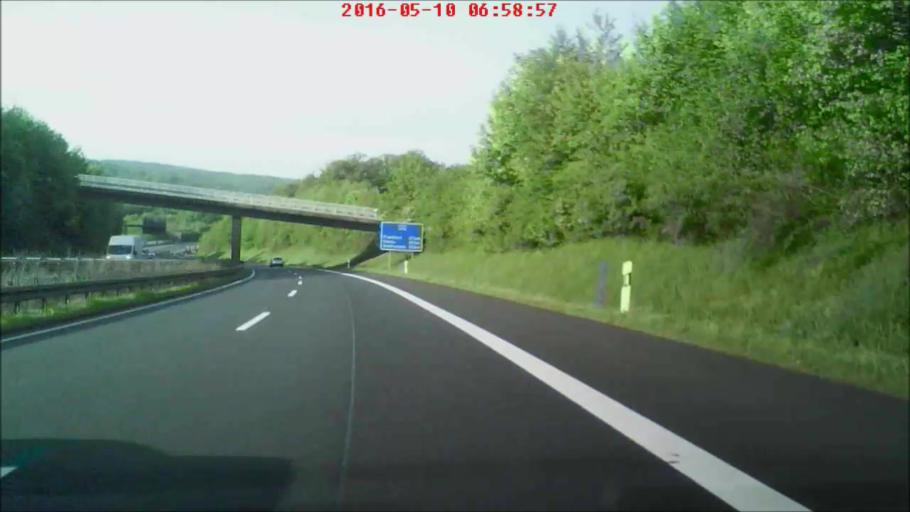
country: DE
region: Hesse
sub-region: Regierungsbezirk Darmstadt
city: Steinau an der Strasse
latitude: 50.3178
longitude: 9.4326
